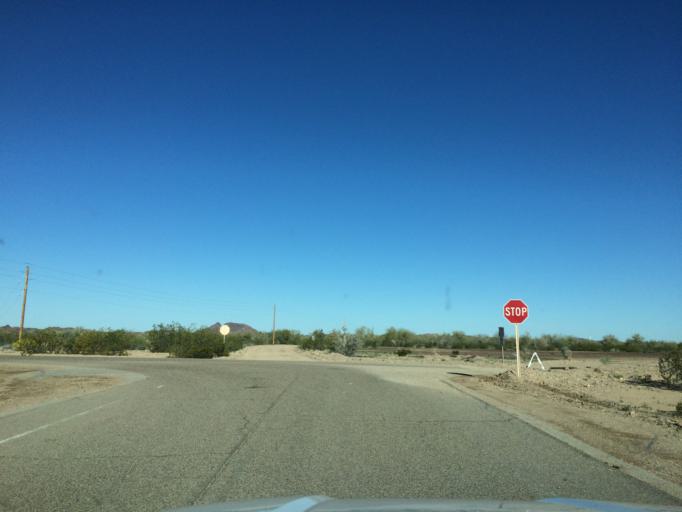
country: US
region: Arizona
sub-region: Yuma County
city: Wellton
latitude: 32.9819
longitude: -114.2715
